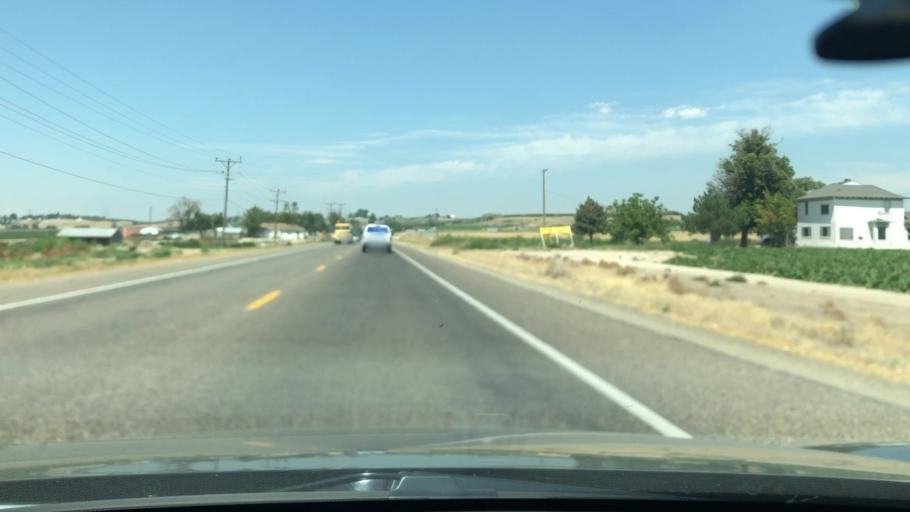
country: US
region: Idaho
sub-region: Canyon County
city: Wilder
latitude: 43.6438
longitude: -116.9117
